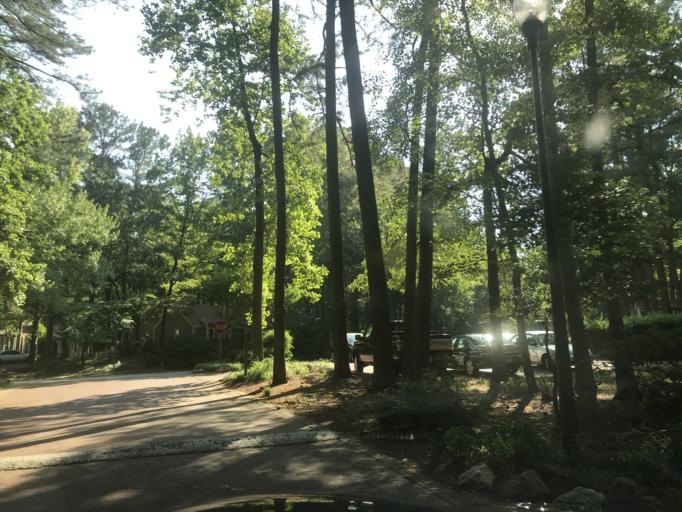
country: US
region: North Carolina
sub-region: Wake County
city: West Raleigh
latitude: 35.8636
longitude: -78.6108
